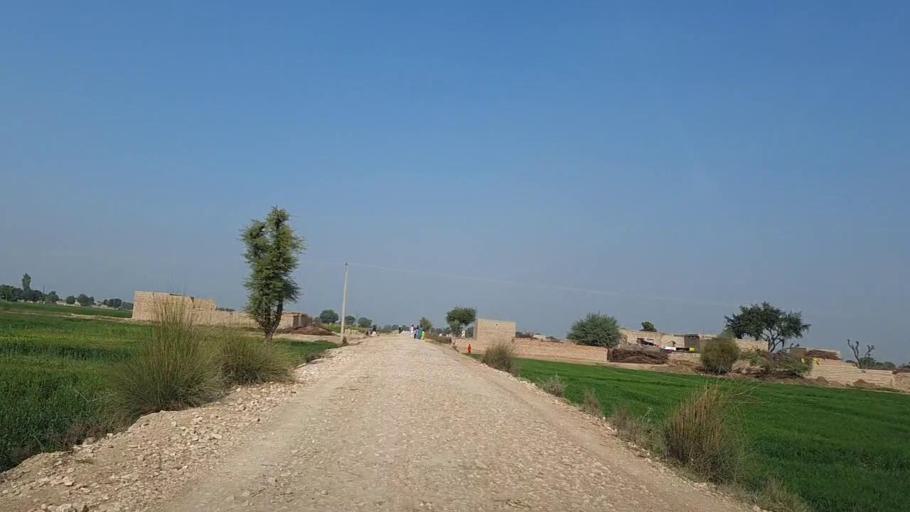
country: PK
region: Sindh
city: Moro
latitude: 26.6918
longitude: 67.9491
